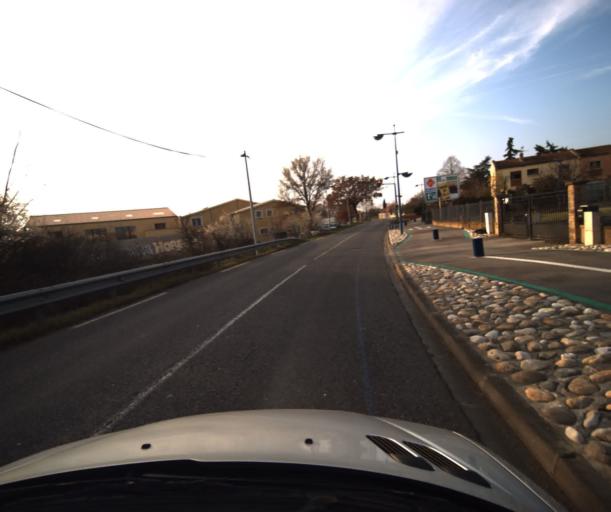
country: FR
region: Midi-Pyrenees
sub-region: Departement de la Haute-Garonne
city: Fonbeauzard
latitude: 43.6833
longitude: 1.4419
